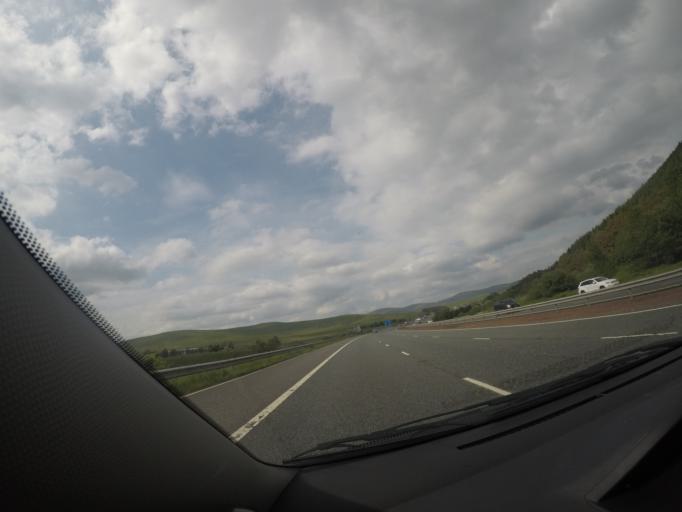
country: GB
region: Scotland
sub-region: South Lanarkshire
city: Biggar
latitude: 55.4443
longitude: -3.6527
